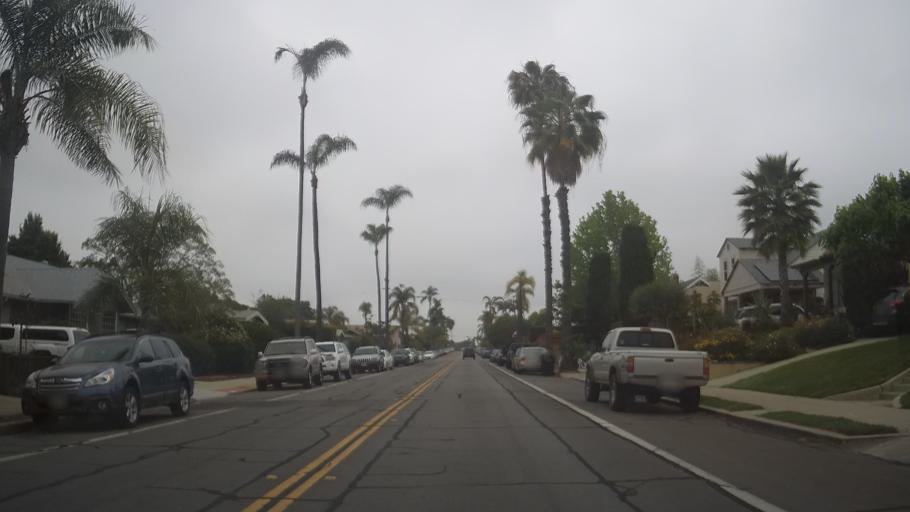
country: US
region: California
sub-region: San Diego County
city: San Diego
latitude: 32.7428
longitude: -117.1390
